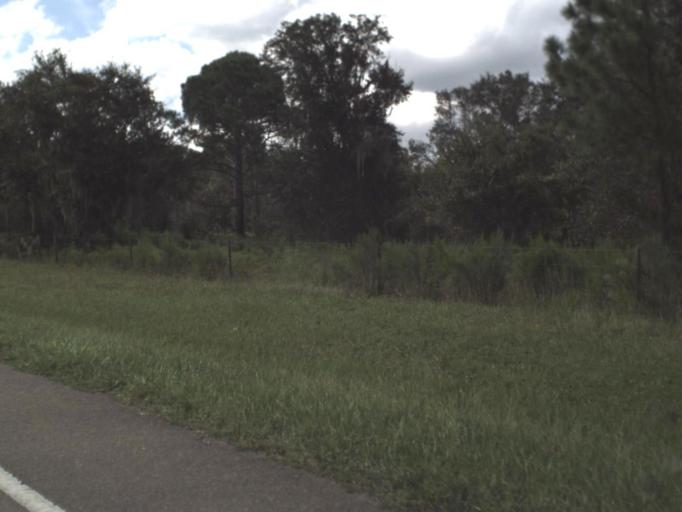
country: US
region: Florida
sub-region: Hardee County
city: Wauchula
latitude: 27.4833
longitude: -81.9351
